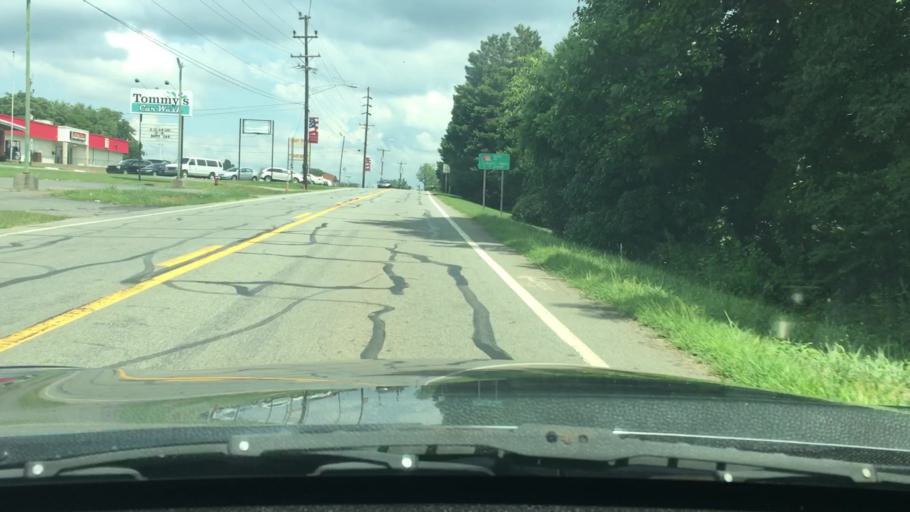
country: US
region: North Carolina
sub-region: Alamance County
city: Mebane
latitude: 36.0981
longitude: -79.2764
